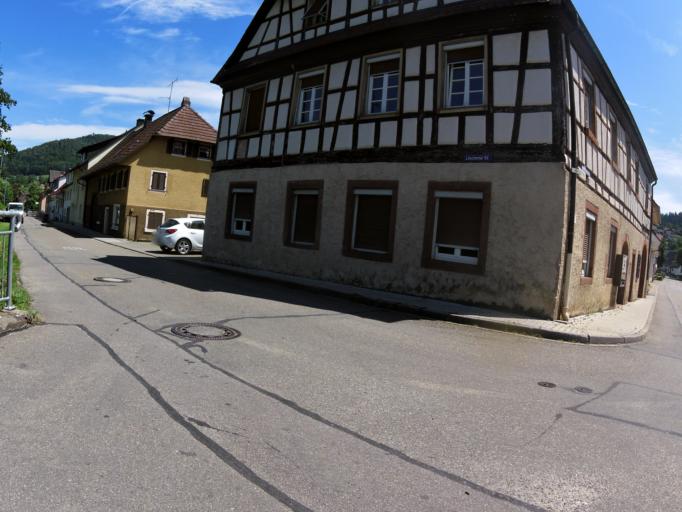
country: DE
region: Baden-Wuerttemberg
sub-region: Freiburg Region
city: Seelbach
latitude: 48.3042
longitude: 7.9380
